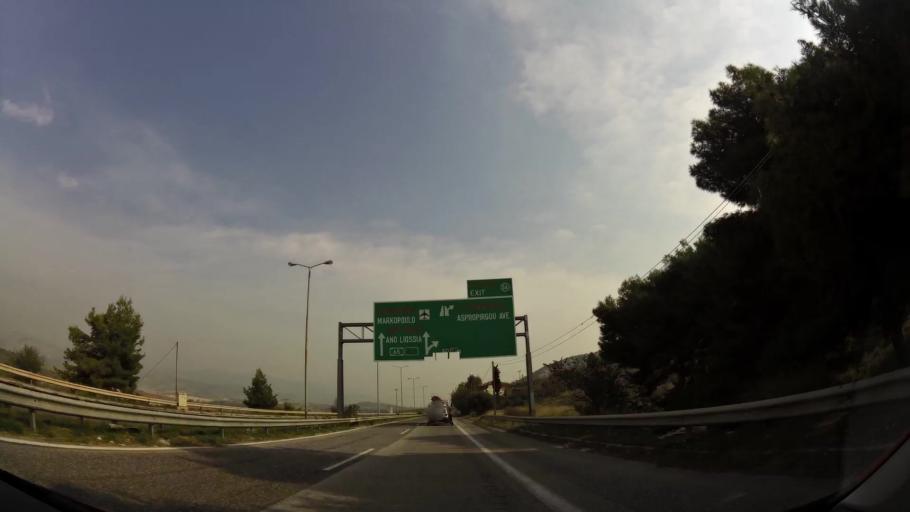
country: GR
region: Attica
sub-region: Nomarchia Athinas
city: Petroupolis
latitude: 38.0503
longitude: 23.6503
